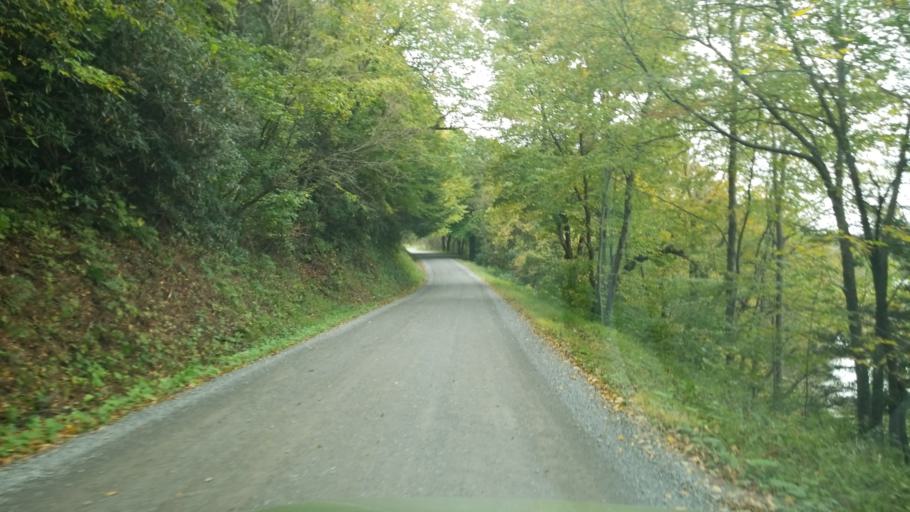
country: US
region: Pennsylvania
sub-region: Clearfield County
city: Curwensville
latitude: 40.9651
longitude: -78.4924
